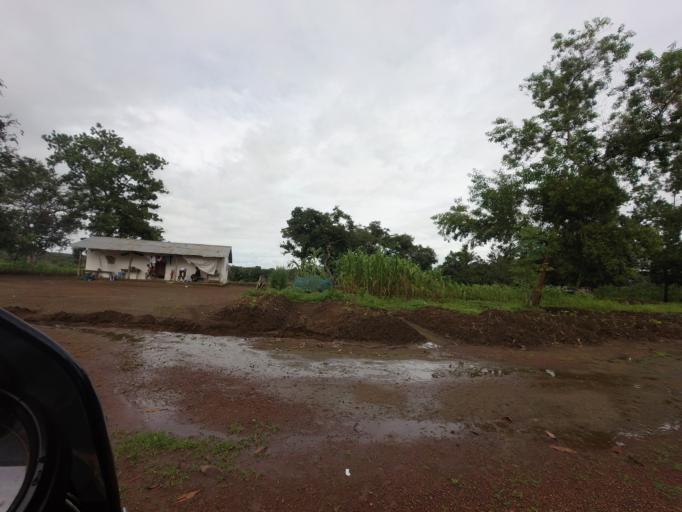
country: SL
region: Northern Province
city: Kambia
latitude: 9.1058
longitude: -12.9199
